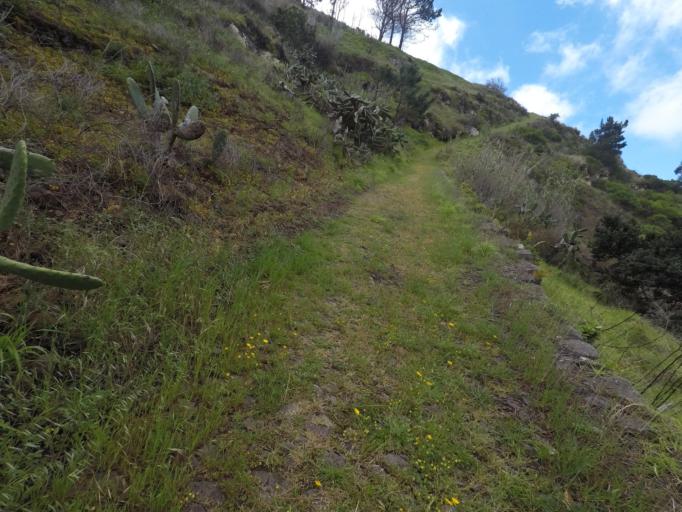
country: PT
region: Madeira
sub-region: Calheta
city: Faja da Ovelha
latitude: 32.7533
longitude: -17.2178
